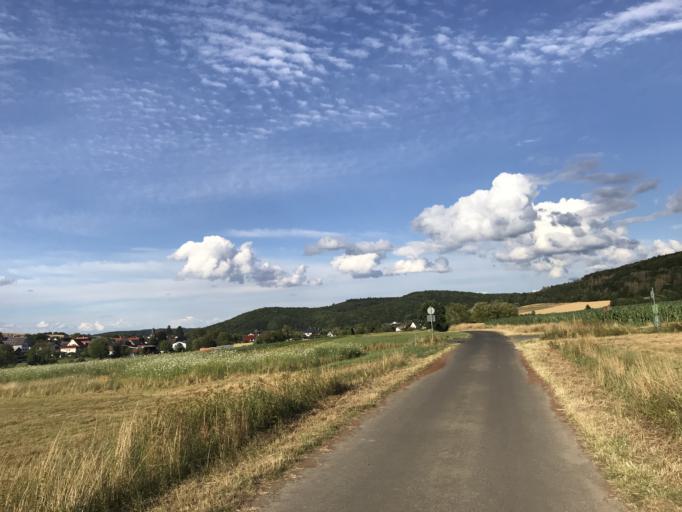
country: DE
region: Hesse
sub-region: Regierungsbezirk Giessen
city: Lohra
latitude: 50.6845
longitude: 8.6012
